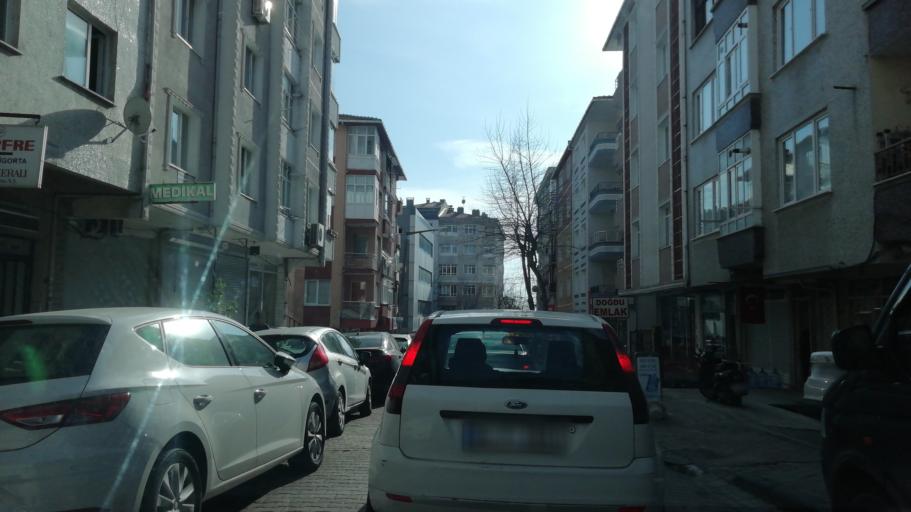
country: TR
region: Istanbul
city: Yakuplu
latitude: 40.9798
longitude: 28.7274
